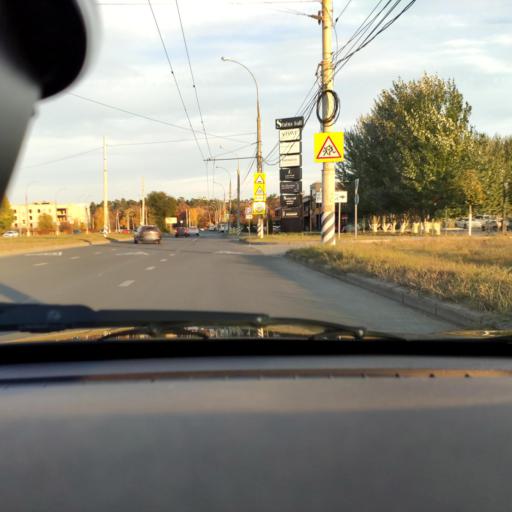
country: RU
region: Samara
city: Tol'yatti
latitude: 53.4979
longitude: 49.2911
